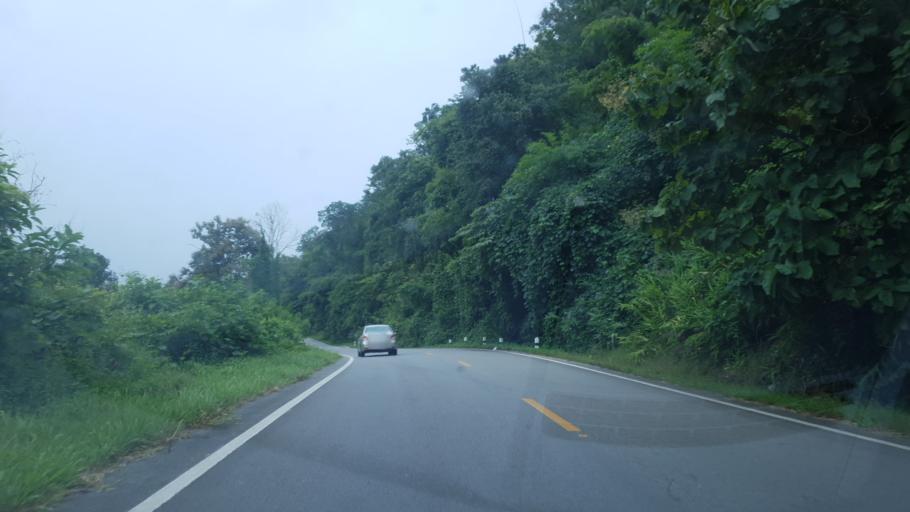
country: TH
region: Mae Hong Son
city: Khun Yuam
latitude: 18.7185
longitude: 97.9083
